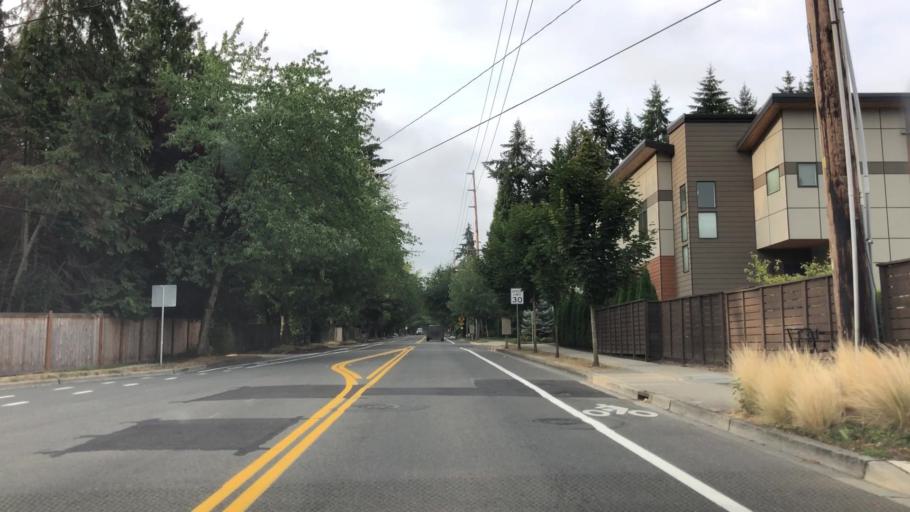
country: US
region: Washington
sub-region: King County
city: Redmond
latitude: 47.6791
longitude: -122.1639
